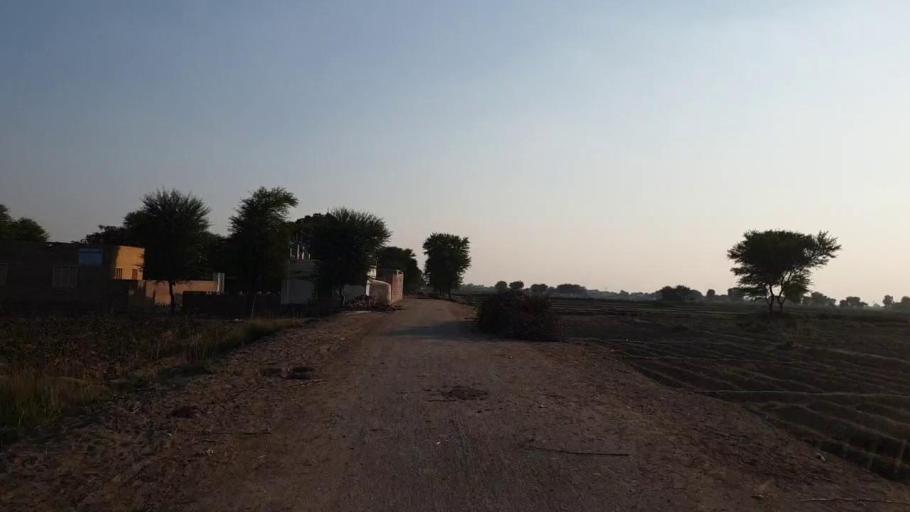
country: PK
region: Sindh
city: Sehwan
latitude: 26.4468
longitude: 67.7840
